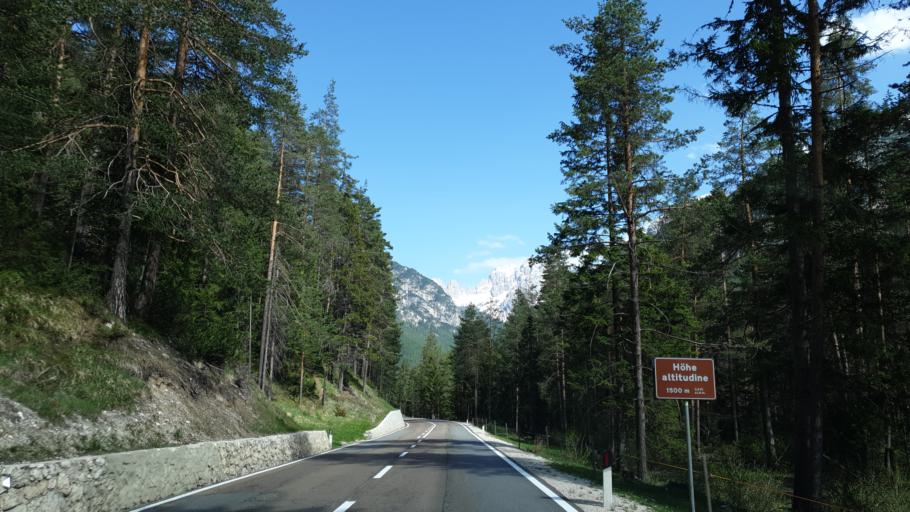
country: IT
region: Veneto
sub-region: Provincia di Belluno
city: Cortina d'Ampezzo
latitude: 46.6235
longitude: 12.1989
